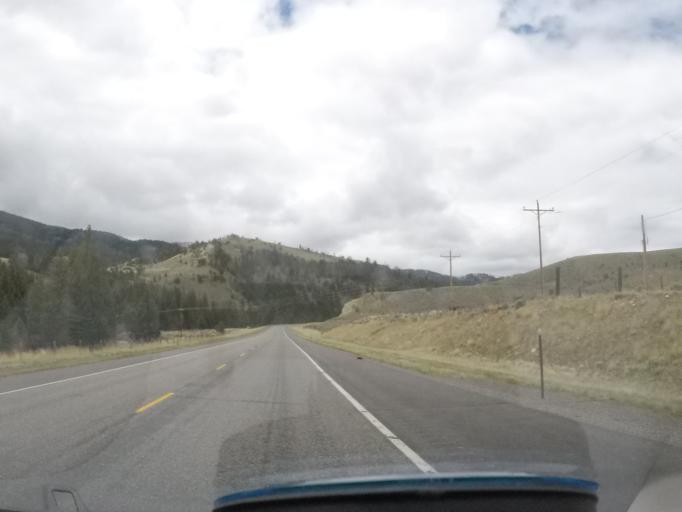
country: US
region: Wyoming
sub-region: Sublette County
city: Pinedale
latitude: 43.5792
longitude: -109.7522
